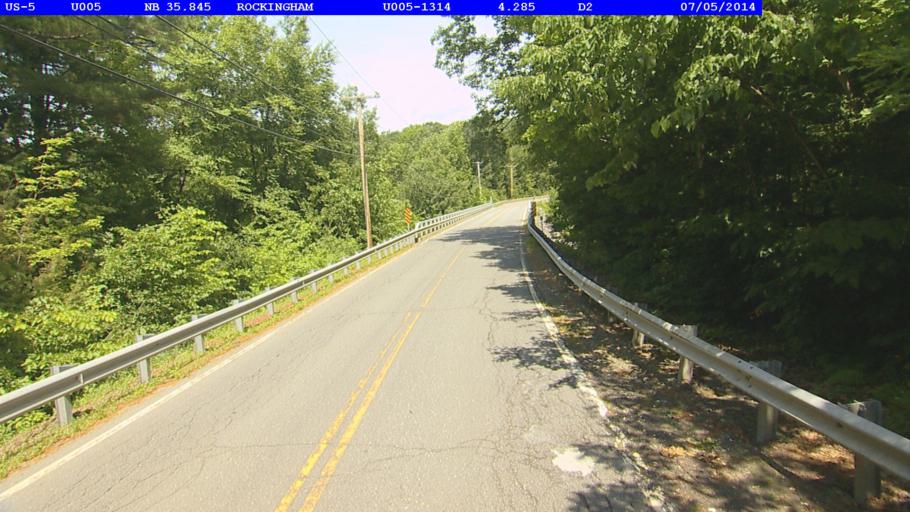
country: US
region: Vermont
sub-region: Windham County
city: Rockingham
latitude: 43.1820
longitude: -72.4601
